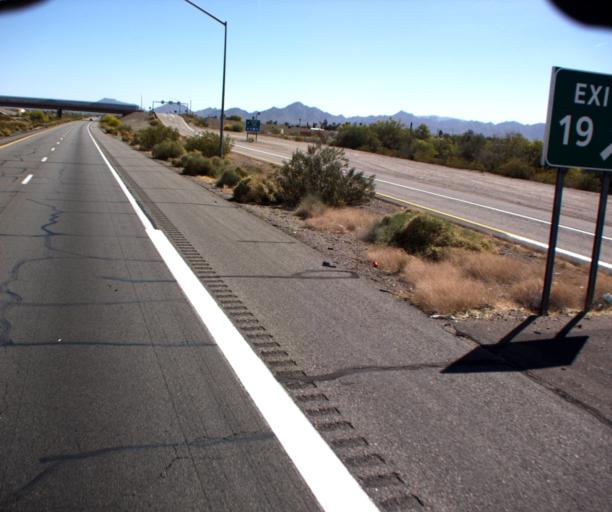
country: US
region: Arizona
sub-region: La Paz County
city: Quartzsite
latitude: 33.6649
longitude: -114.2039
